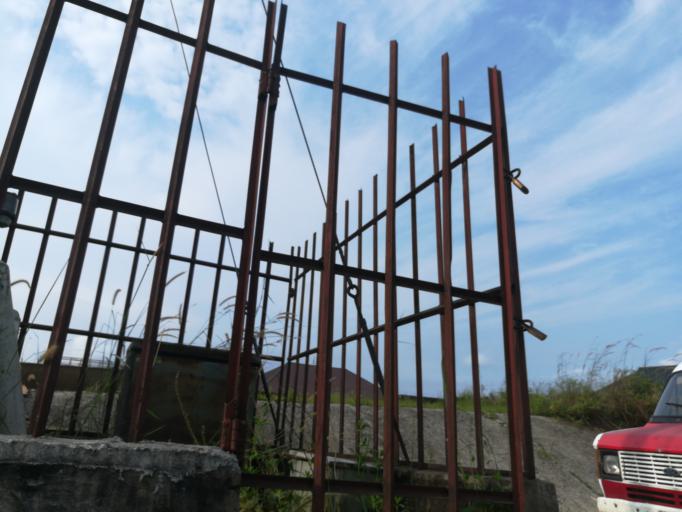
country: NG
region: Rivers
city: Okrika
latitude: 4.7317
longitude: 7.0814
